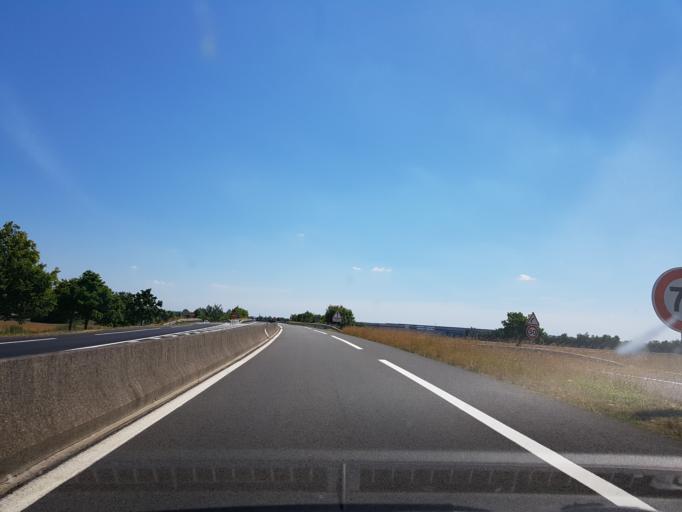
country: FR
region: Picardie
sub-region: Departement de l'Aisne
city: Holnon
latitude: 49.8453
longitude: 3.2313
